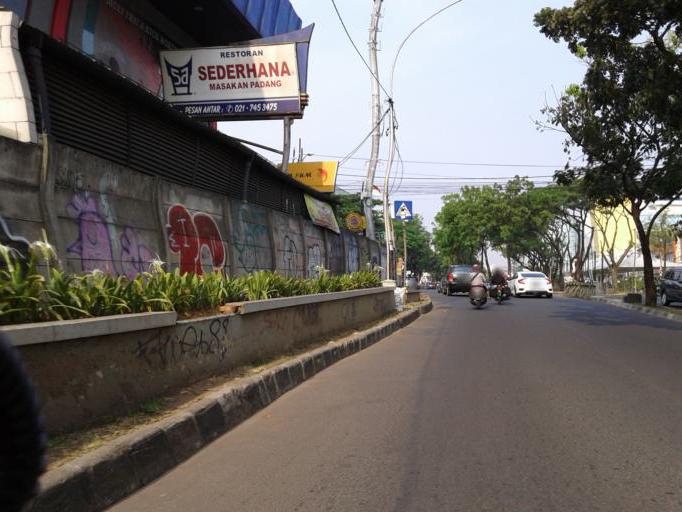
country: ID
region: Banten
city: South Tangerang
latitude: -6.2793
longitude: 106.7182
